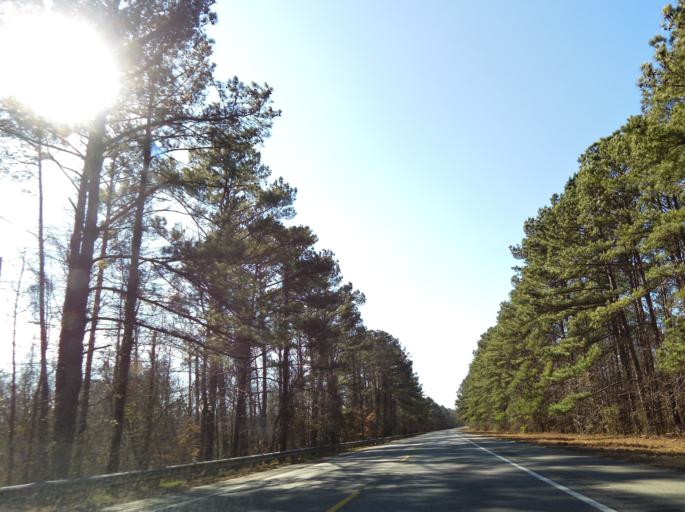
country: US
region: Georgia
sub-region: Bibb County
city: West Point
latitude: 32.7978
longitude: -83.7631
